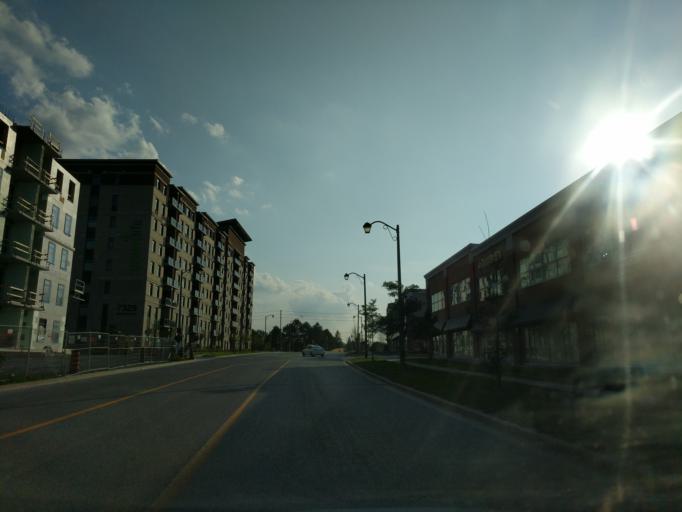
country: CA
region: Ontario
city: Markham
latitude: 43.8486
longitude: -79.2515
